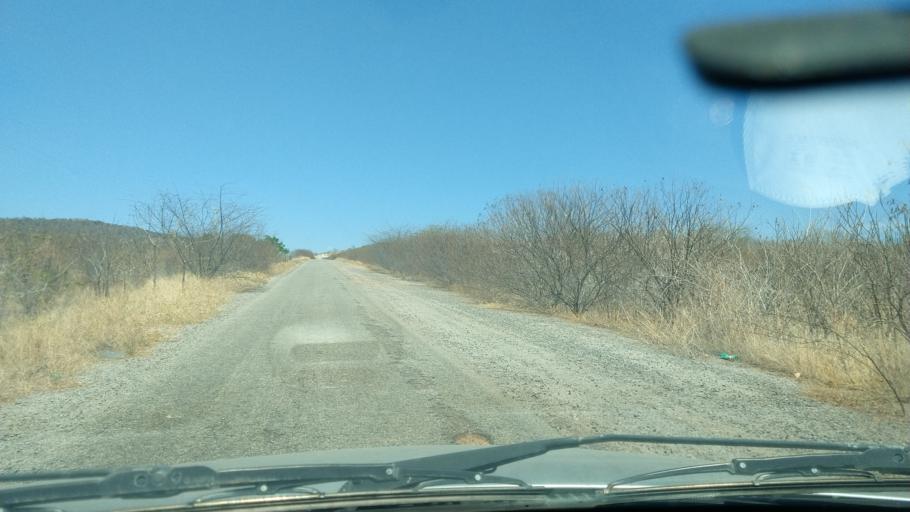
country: BR
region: Rio Grande do Norte
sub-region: Sao Tome
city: Sao Tome
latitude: -5.9752
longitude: -36.1503
